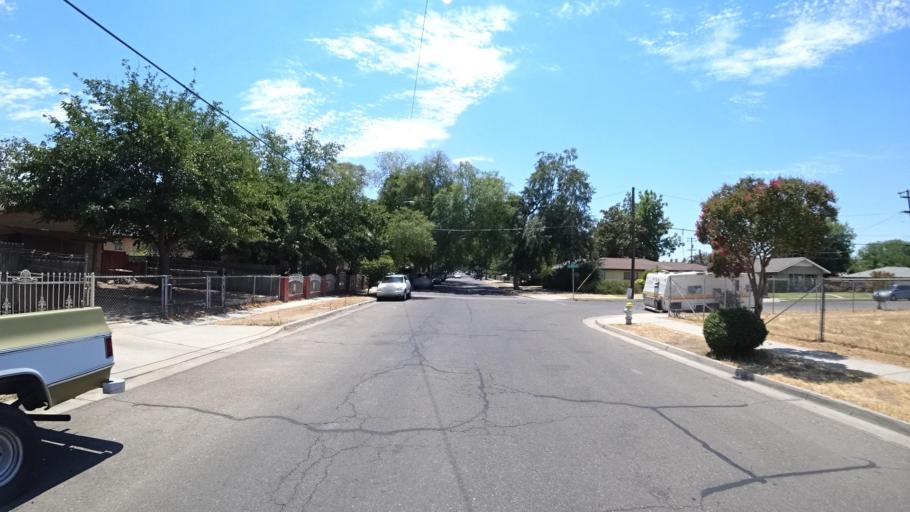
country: US
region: California
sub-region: Fresno County
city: Fresno
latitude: 36.7345
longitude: -119.7613
